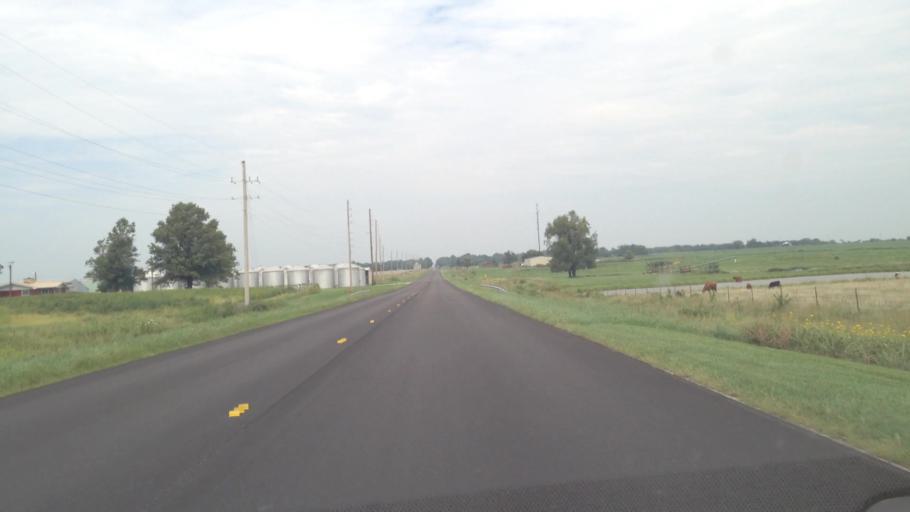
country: US
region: Kansas
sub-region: Allen County
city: Iola
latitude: 37.8937
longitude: -95.1701
